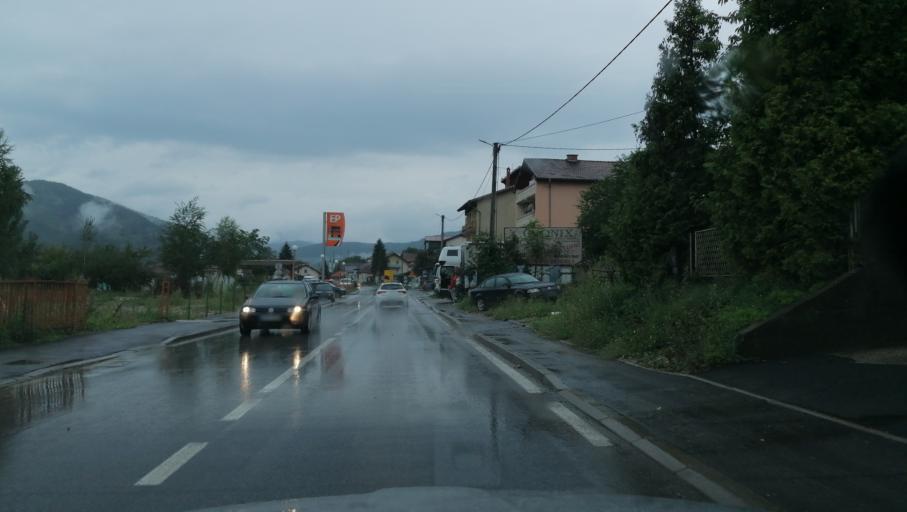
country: BA
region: Federation of Bosnia and Herzegovina
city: Gorazde
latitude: 43.6741
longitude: 18.9835
